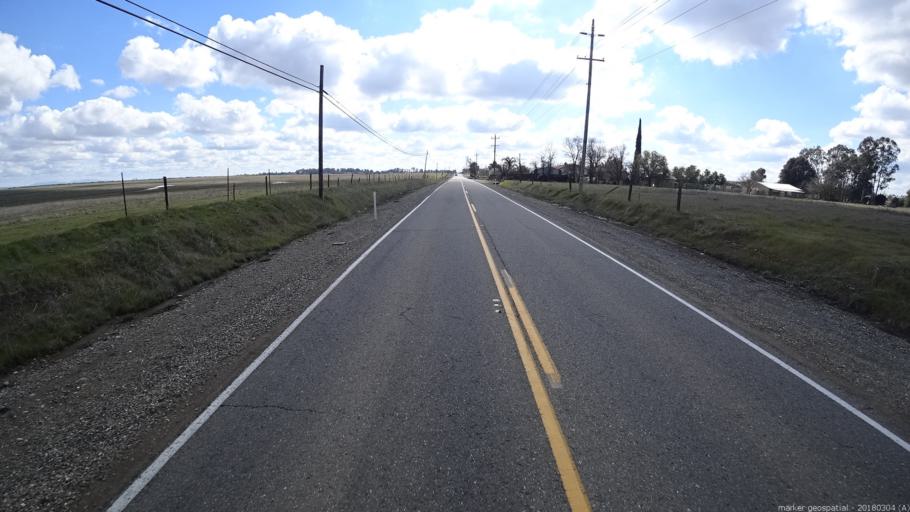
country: US
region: California
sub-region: Sacramento County
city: Vineyard
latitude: 38.4810
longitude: -121.2976
